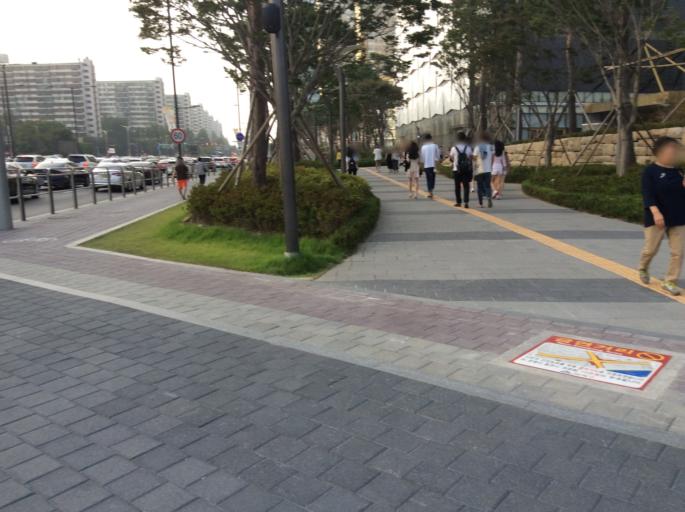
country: KR
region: Gyeonggi-do
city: Seongnam-si
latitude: 37.5115
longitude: 127.1020
